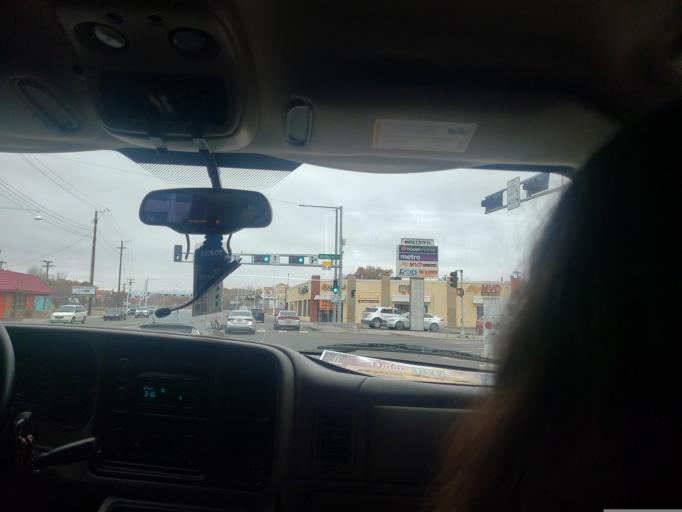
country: US
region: New Mexico
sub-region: Bernalillo County
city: Albuquerque
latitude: 35.0852
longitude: -106.6862
